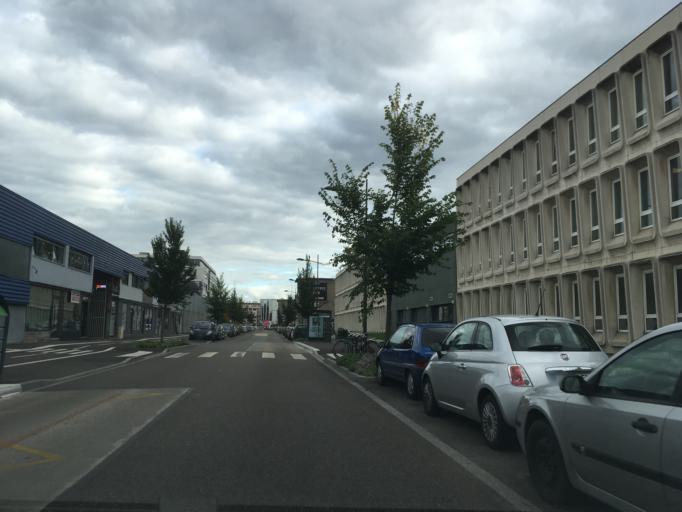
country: FR
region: Alsace
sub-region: Departement du Bas-Rhin
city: Strasbourg
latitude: 48.5605
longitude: 7.7435
